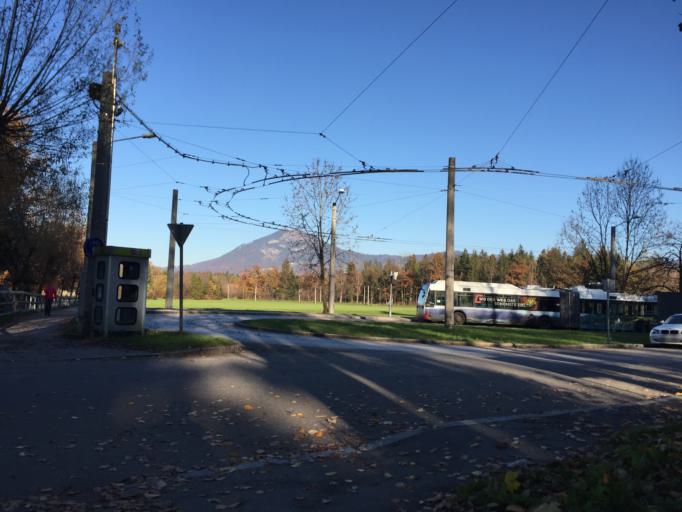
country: AT
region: Salzburg
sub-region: Politischer Bezirk Salzburg-Umgebung
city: Grodig
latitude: 47.7602
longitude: 13.0366
